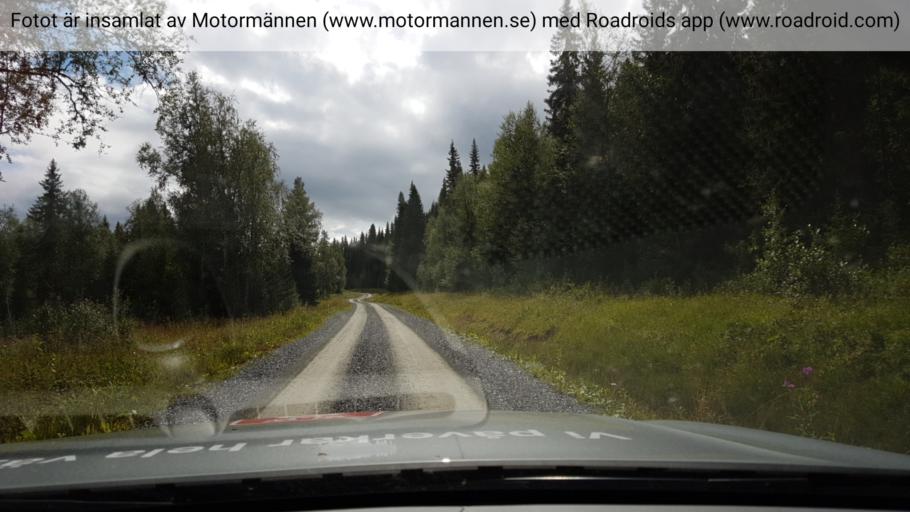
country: SE
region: Jaemtland
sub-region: Krokoms Kommun
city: Valla
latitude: 63.5295
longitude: 13.9021
